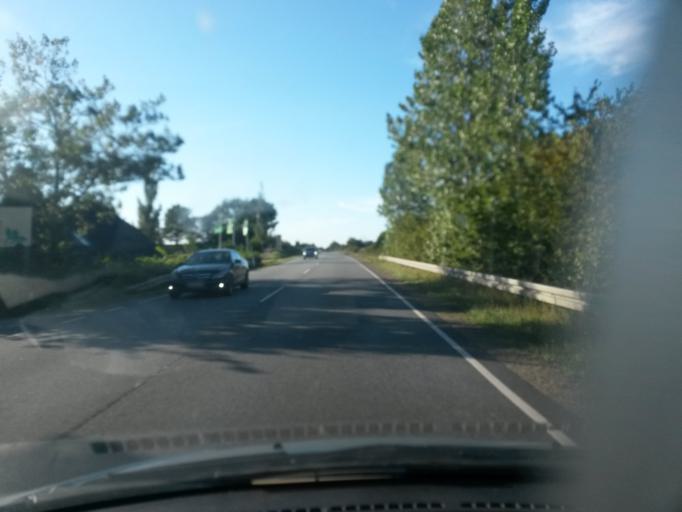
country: DK
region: Central Jutland
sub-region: Favrskov Kommune
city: Hammel
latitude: 56.2528
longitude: 9.7652
